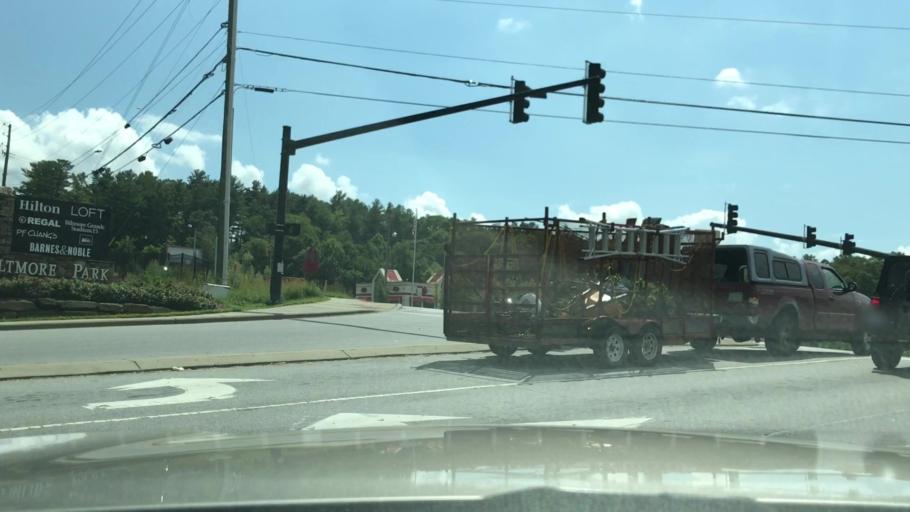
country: US
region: North Carolina
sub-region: Buncombe County
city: Avery Creek
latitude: 35.4823
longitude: -82.5532
